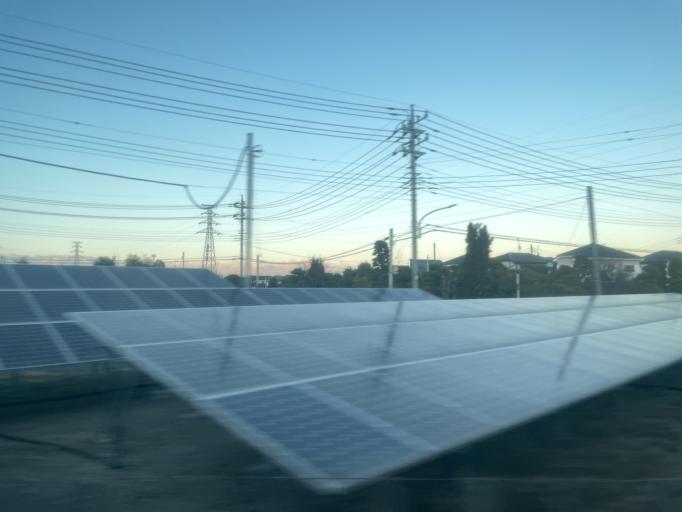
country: JP
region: Saitama
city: Honjo
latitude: 36.2104
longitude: 139.2287
